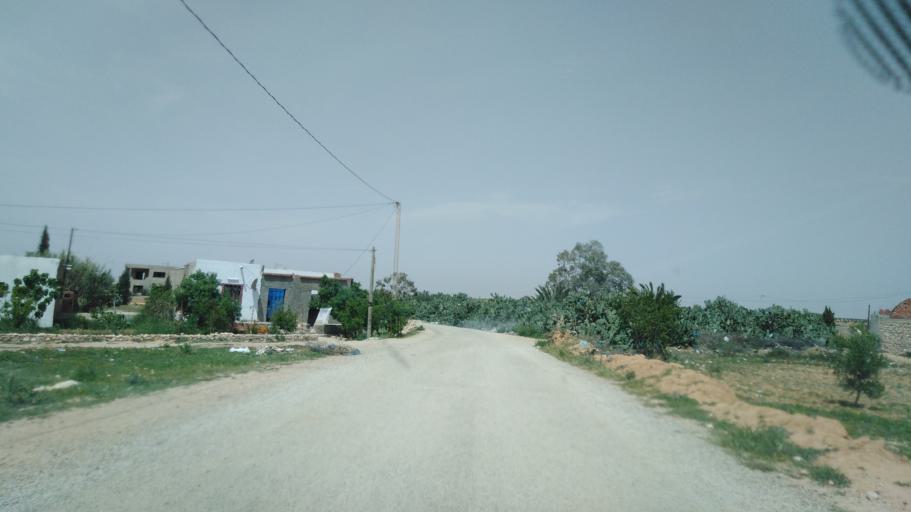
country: TN
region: Safaqis
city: Sfax
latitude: 34.7288
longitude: 10.5535
